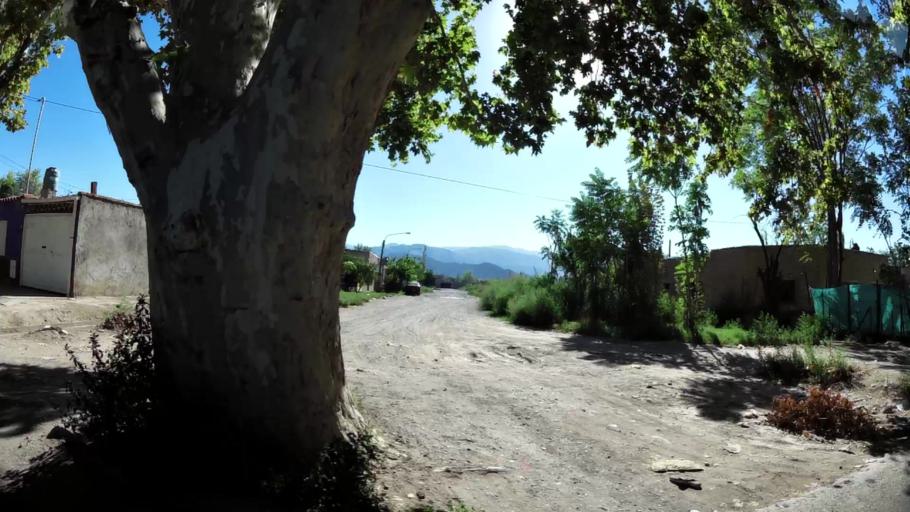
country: AR
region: Mendoza
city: Las Heras
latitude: -32.8363
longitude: -68.8248
